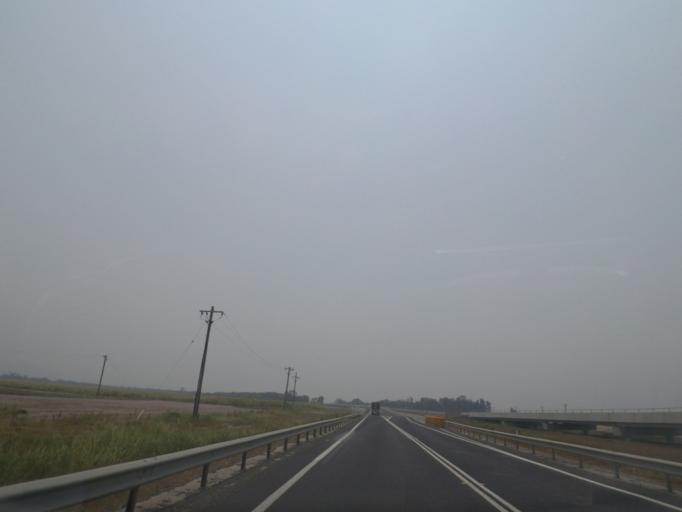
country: AU
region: New South Wales
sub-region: Clarence Valley
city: Maclean
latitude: -29.4088
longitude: 153.2421
